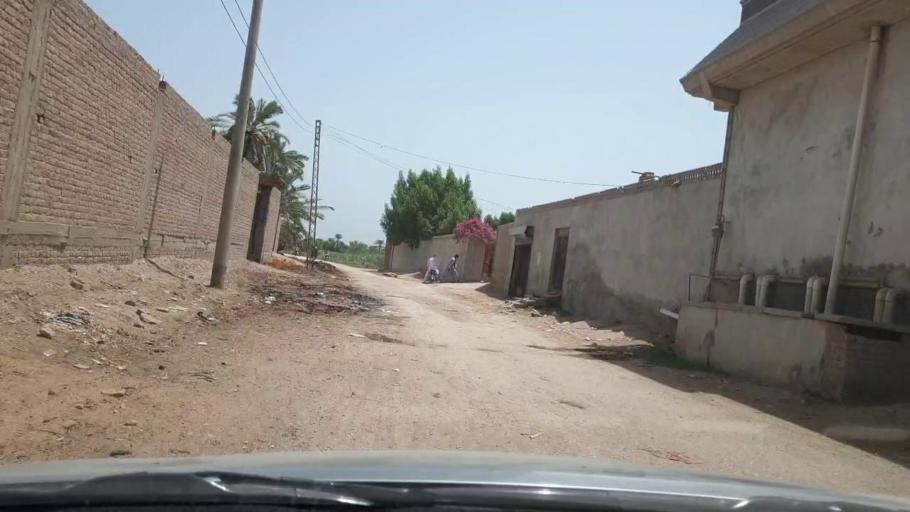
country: PK
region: Sindh
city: Pano Aqil
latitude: 27.8599
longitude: 69.0721
